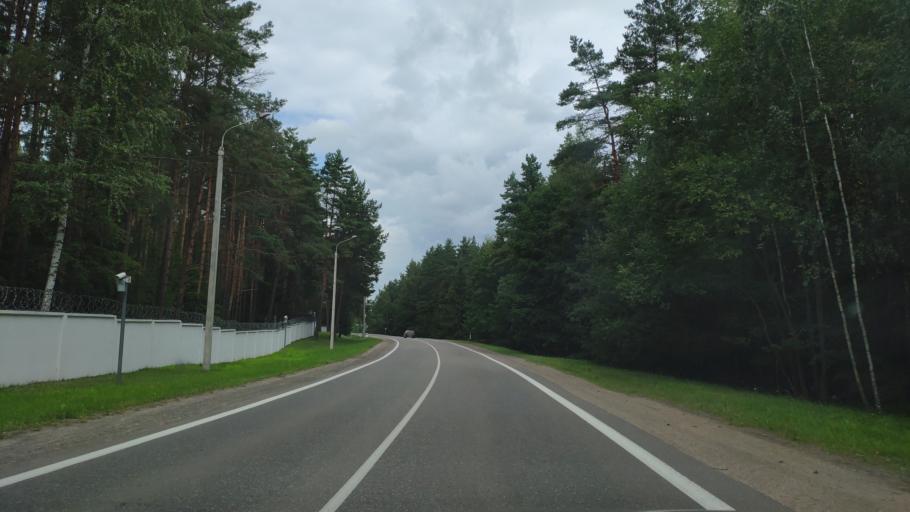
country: BY
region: Minsk
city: Syomkava
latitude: 53.9833
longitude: 27.4558
